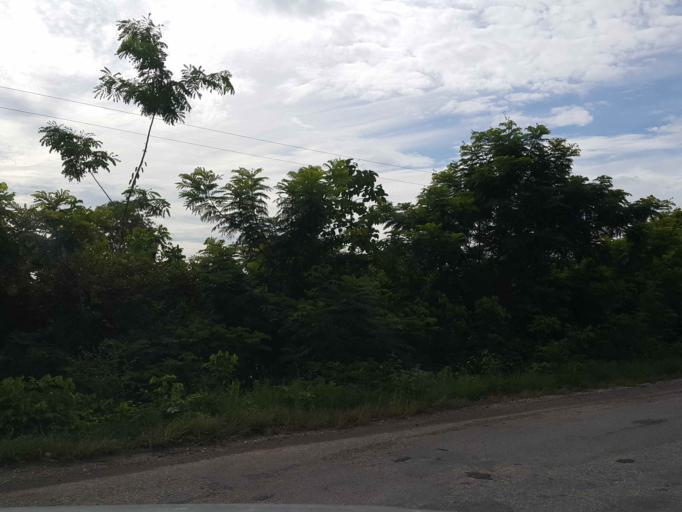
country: TH
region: Sukhothai
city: Thung Saliam
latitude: 17.3041
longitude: 99.5267
